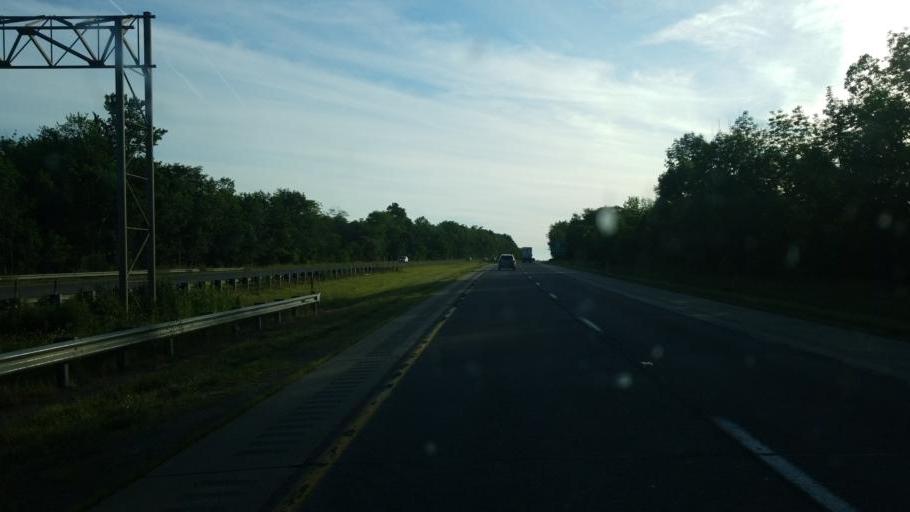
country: US
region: Pennsylvania
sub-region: Erie County
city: Fairview
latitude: 42.0238
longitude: -80.1439
